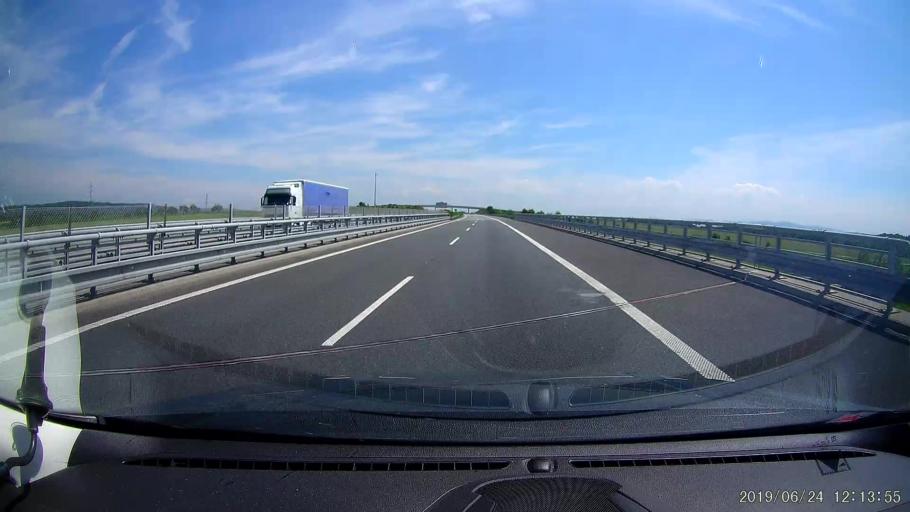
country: CZ
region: Olomoucky
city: Belotin
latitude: 49.5874
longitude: 17.7681
